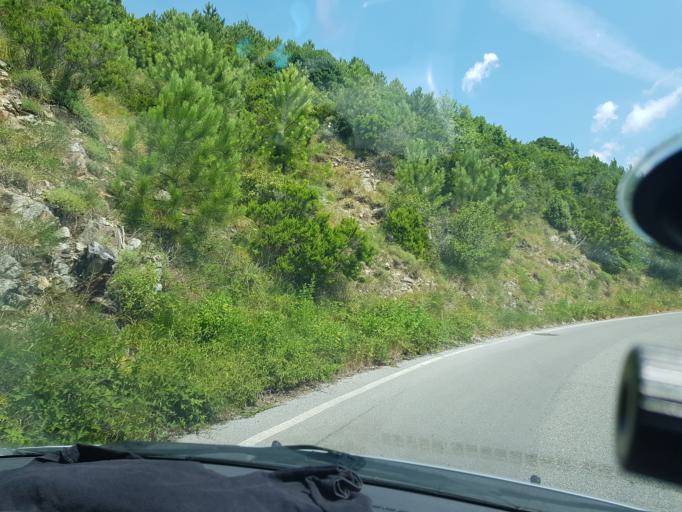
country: IT
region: Liguria
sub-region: Provincia di Genova
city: San Teodoro
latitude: 44.4409
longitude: 8.8389
